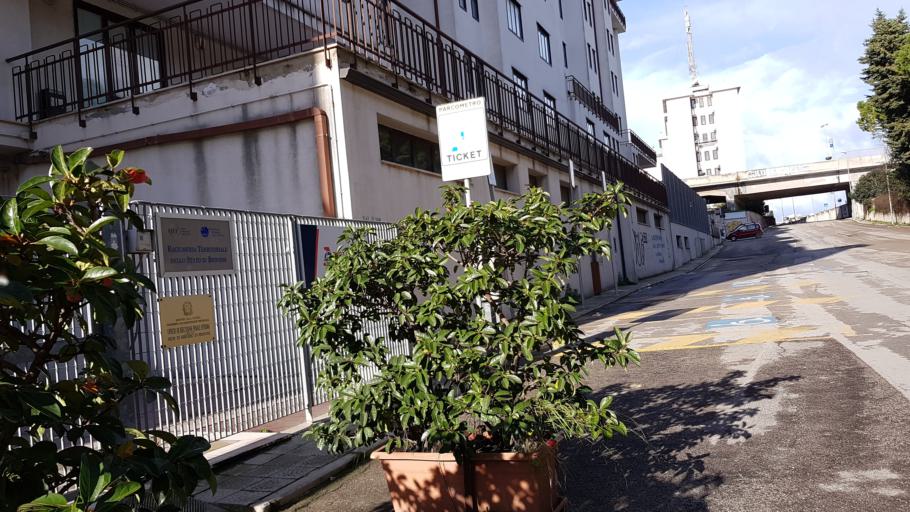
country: IT
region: Apulia
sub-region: Provincia di Brindisi
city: Brindisi
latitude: 40.6300
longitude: 17.9413
